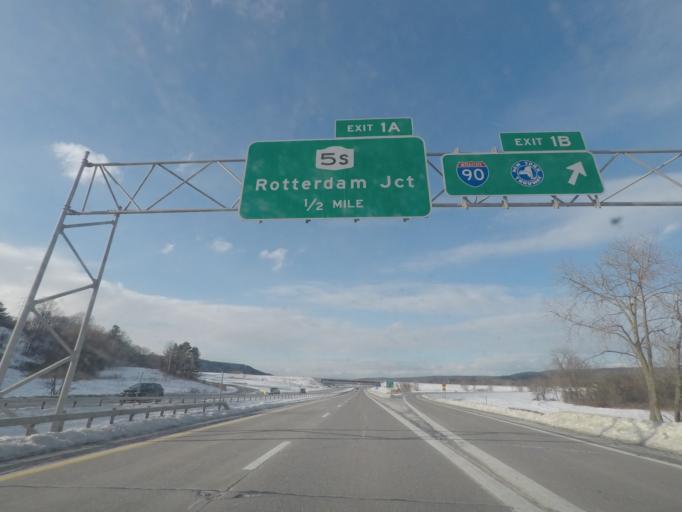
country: US
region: New York
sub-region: Schenectady County
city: Scotia
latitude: 42.8384
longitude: -74.0009
